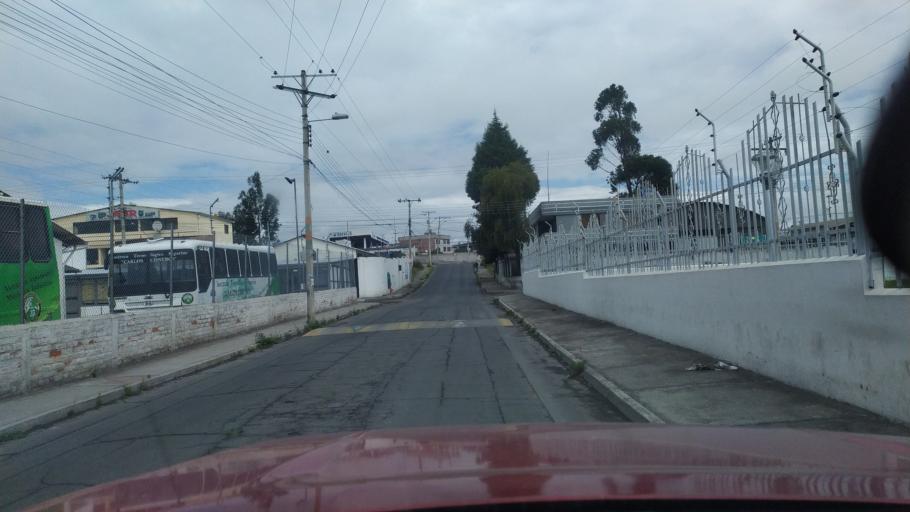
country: EC
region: Chimborazo
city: Riobamba
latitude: -1.6778
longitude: -78.6366
